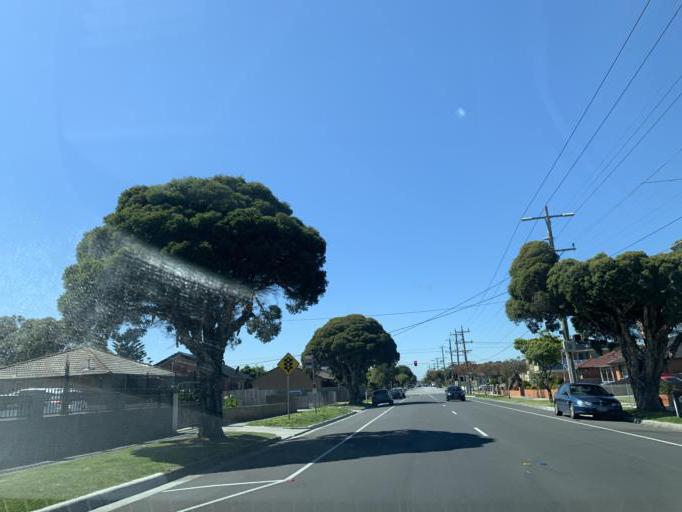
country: AU
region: Victoria
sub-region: Greater Dandenong
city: Dandenong
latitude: -37.9986
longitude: 145.2073
